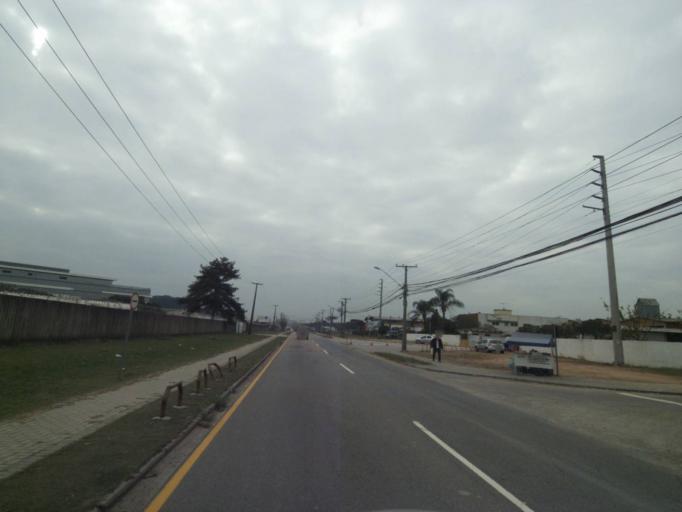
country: BR
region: Parana
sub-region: Curitiba
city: Curitiba
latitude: -25.5196
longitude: -49.3264
